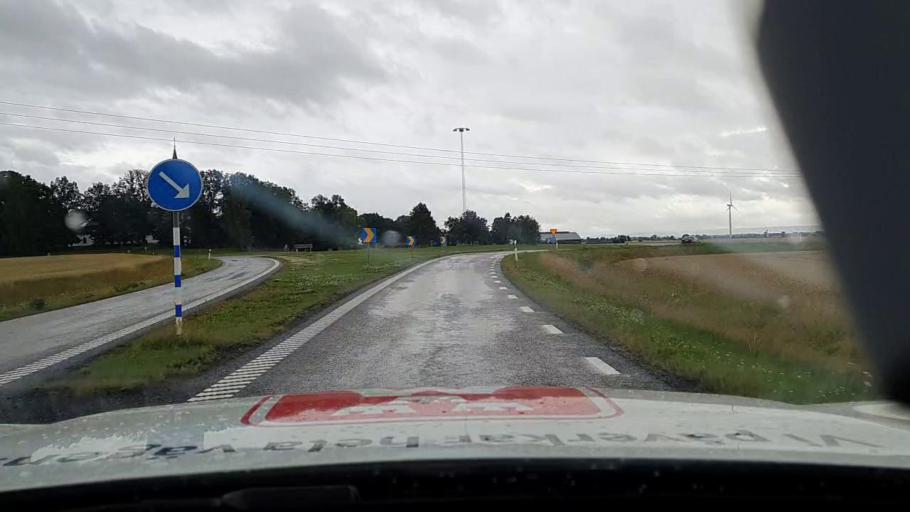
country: SE
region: Vaestra Goetaland
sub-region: Toreboda Kommun
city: Toereboda
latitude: 58.6098
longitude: 14.0106
